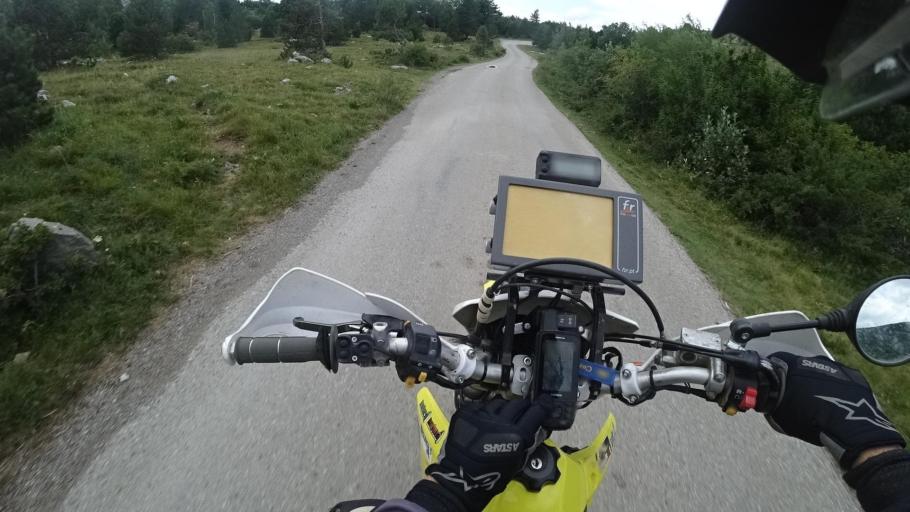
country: HR
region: Licko-Senjska
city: Senj
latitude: 45.1038
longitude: 14.9079
